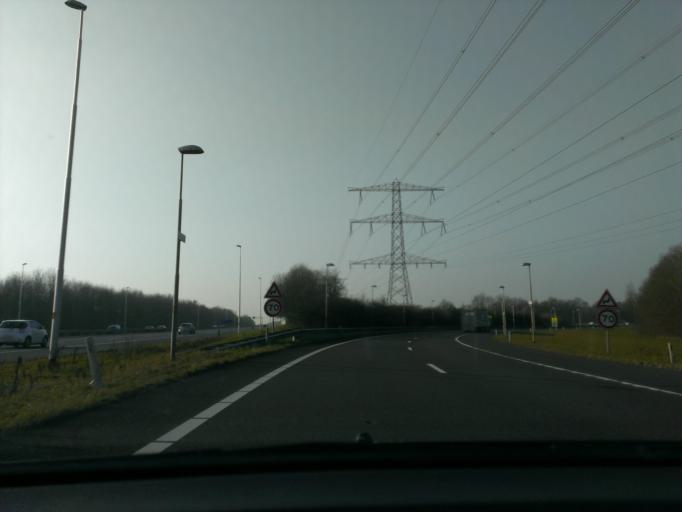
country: NL
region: Overijssel
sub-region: Gemeente Borne
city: Borne
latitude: 52.3081
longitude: 6.7043
